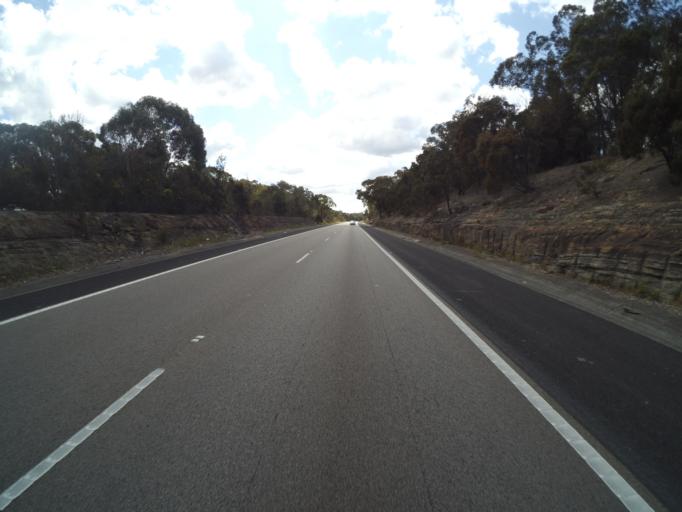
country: AU
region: New South Wales
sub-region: Wingecarribee
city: Colo Vale
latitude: -34.3850
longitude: 150.5234
